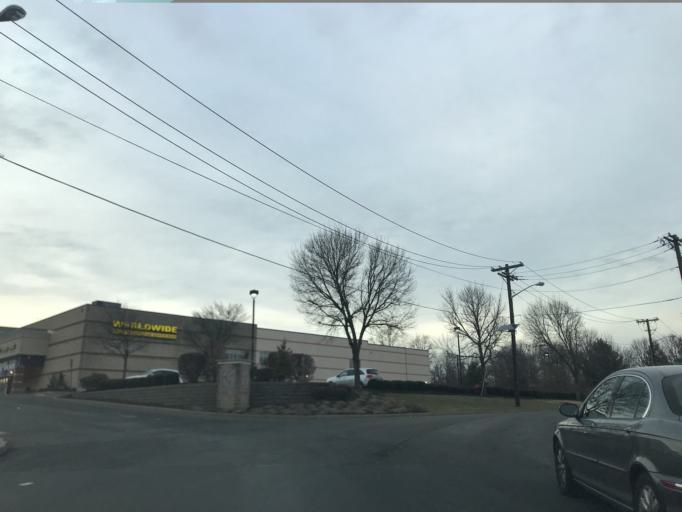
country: US
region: New Jersey
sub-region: Middlesex County
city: Metuchen
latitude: 40.5240
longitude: -74.3613
